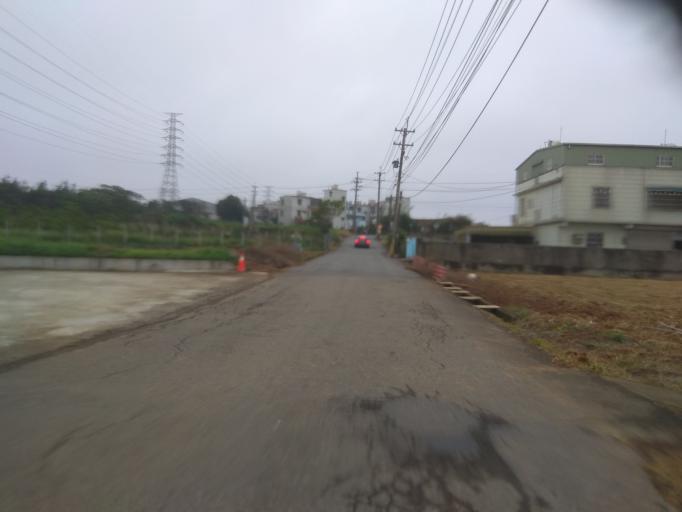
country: TW
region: Taiwan
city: Taoyuan City
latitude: 24.9927
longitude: 121.1254
